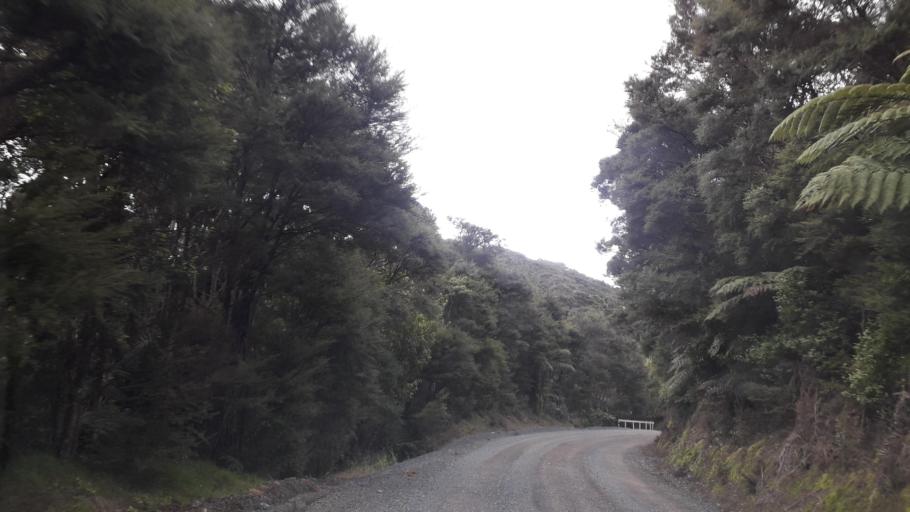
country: NZ
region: Northland
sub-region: Far North District
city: Paihia
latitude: -35.3216
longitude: 174.2342
